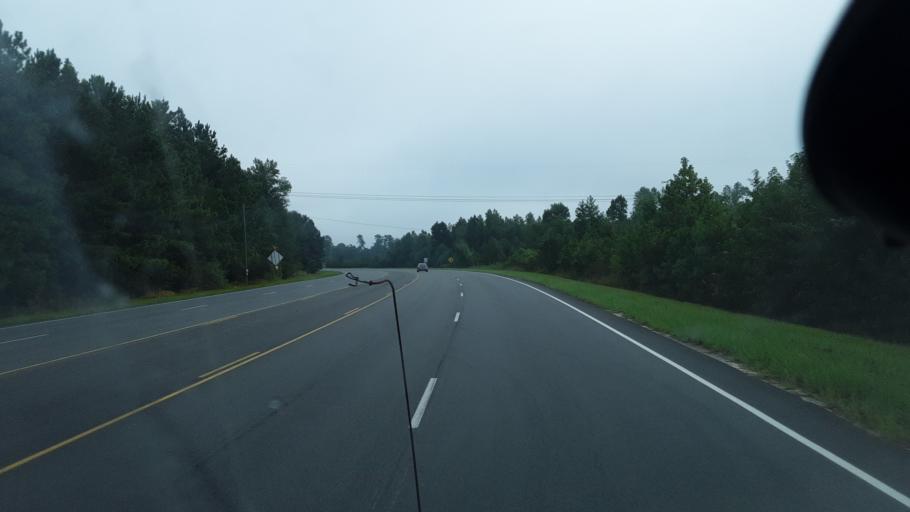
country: US
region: South Carolina
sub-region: Florence County
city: Johnsonville
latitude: 33.8844
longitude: -79.4505
